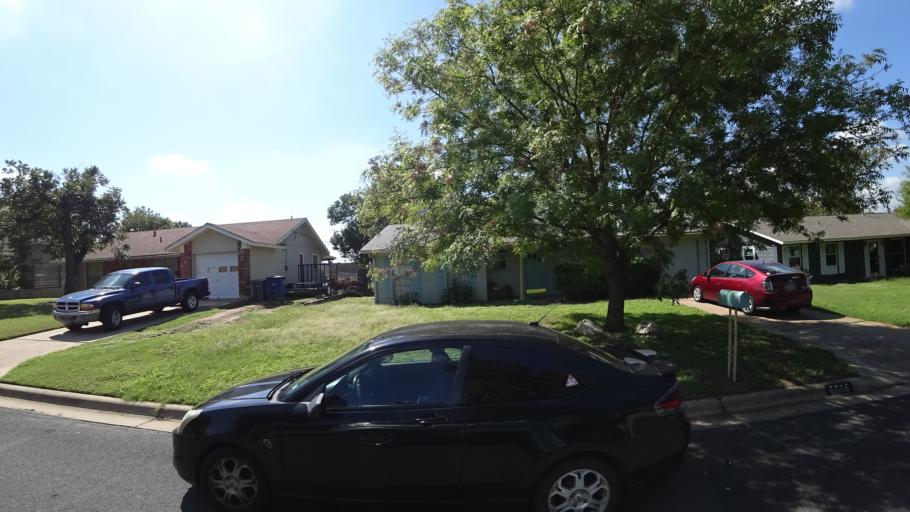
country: US
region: Texas
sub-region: Travis County
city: Austin
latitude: 30.3316
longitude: -97.7139
